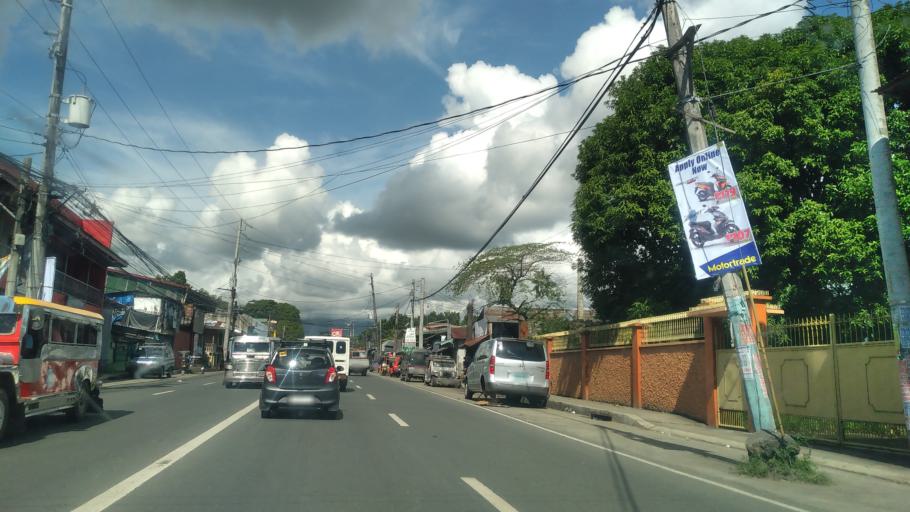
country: PH
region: Calabarzon
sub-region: Province of Quezon
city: Lucena
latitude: 13.9401
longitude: 121.5967
